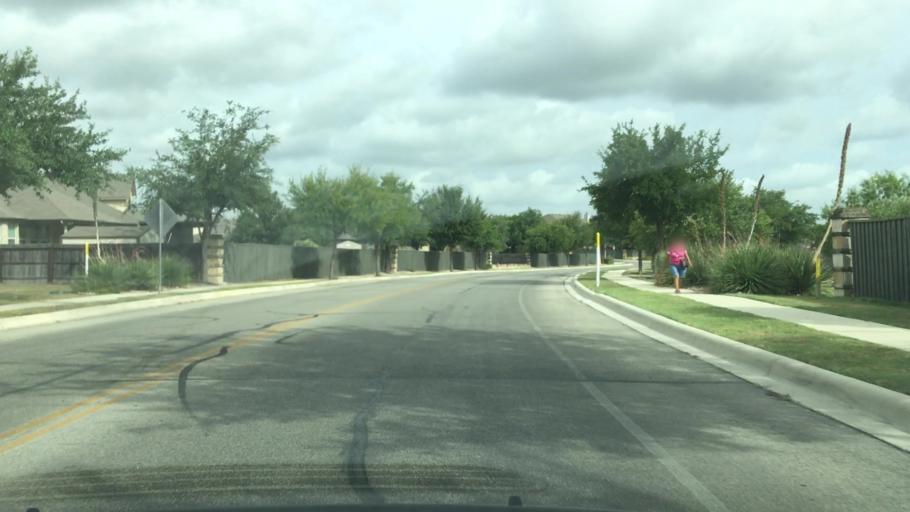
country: US
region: Texas
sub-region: Guadalupe County
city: Cibolo
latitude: 29.5776
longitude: -98.2391
